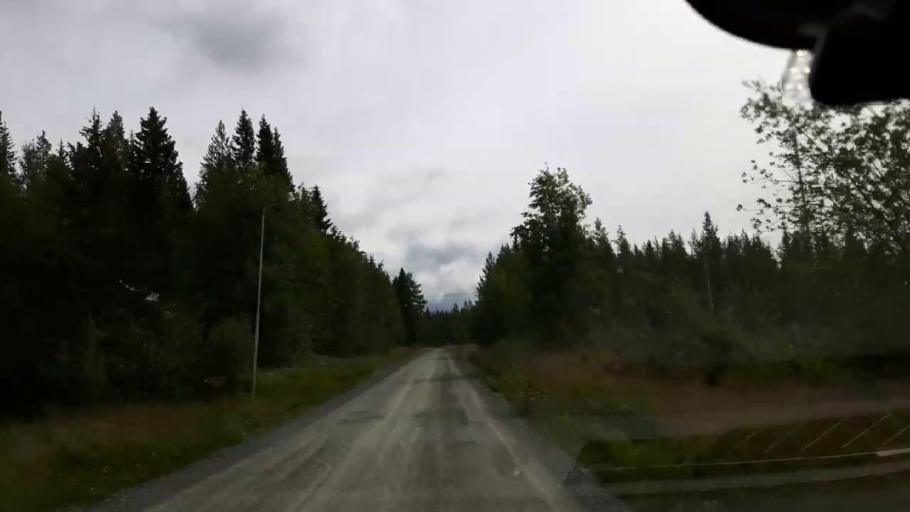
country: SE
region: Jaemtland
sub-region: Krokoms Kommun
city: Valla
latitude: 63.6424
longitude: 13.9952
